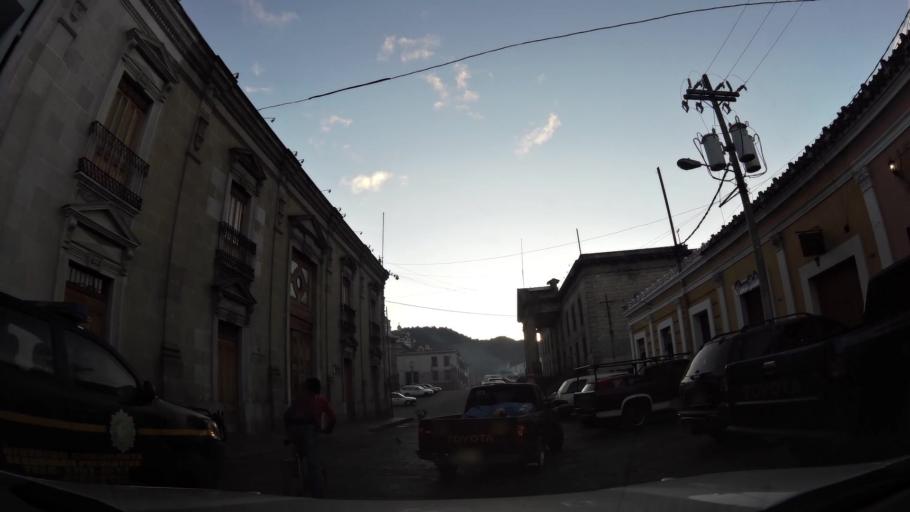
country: GT
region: Quetzaltenango
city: Quetzaltenango
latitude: 14.8337
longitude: -91.5192
